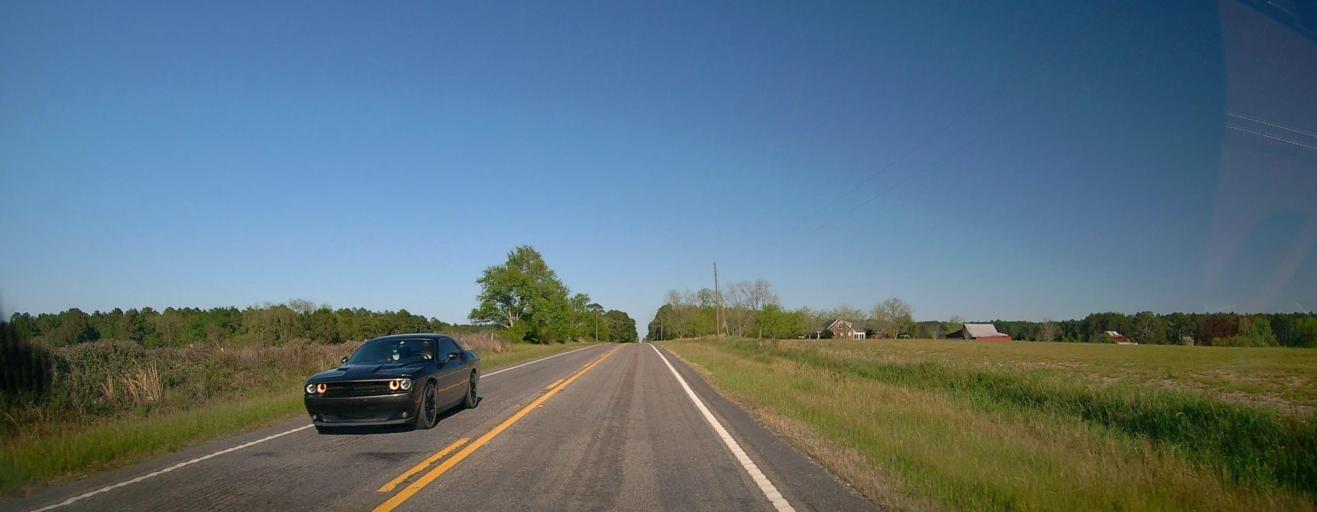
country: US
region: Georgia
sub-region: Ben Hill County
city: Fitzgerald
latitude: 31.7188
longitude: -83.3523
